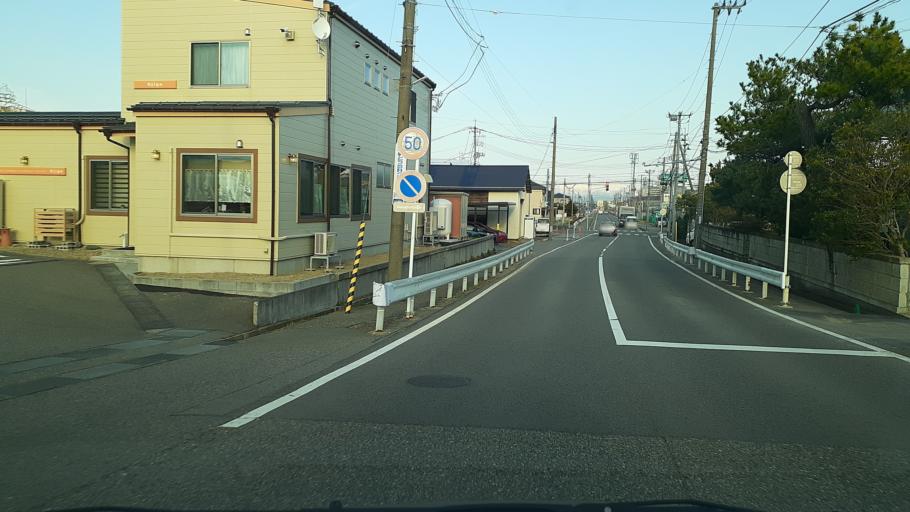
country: JP
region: Niigata
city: Niigata-shi
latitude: 37.8676
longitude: 139.0264
